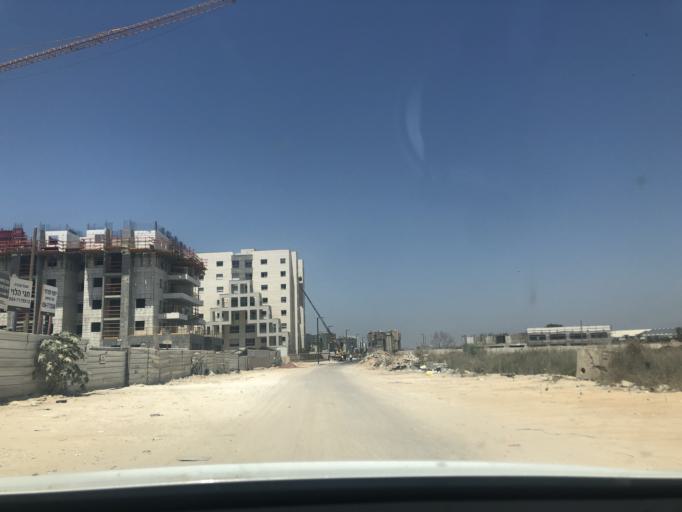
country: IL
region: Central District
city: Lod
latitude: 31.9384
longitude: 34.9008
